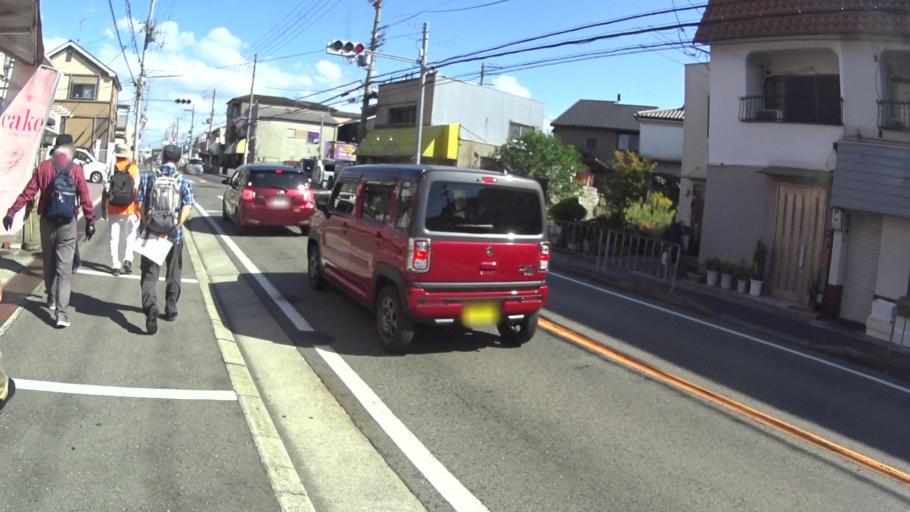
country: JP
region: Ehime
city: Kihoku-cho
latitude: 33.3727
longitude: 132.8024
